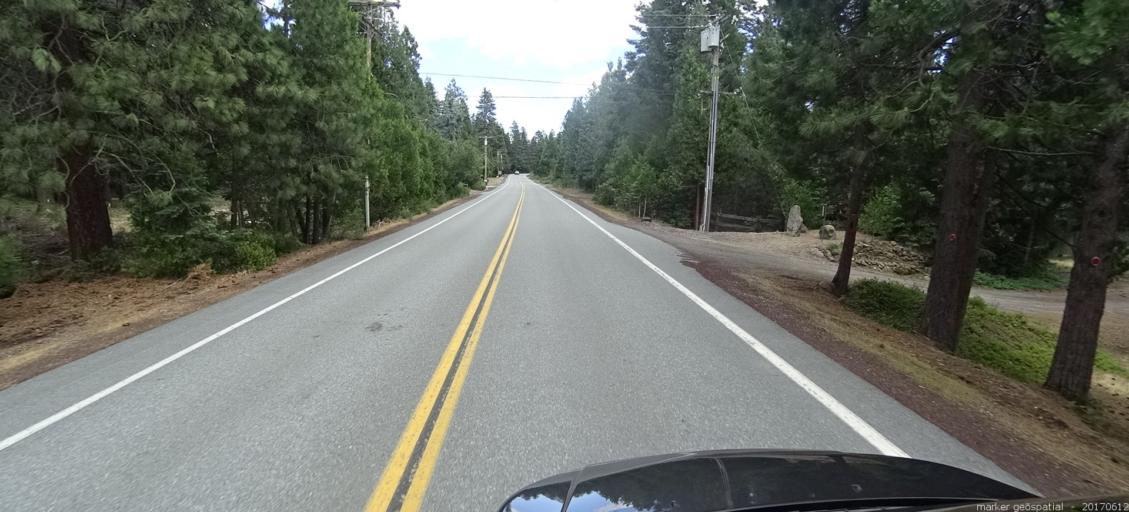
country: US
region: California
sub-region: Siskiyou County
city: Mount Shasta
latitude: 41.3458
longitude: -122.3614
